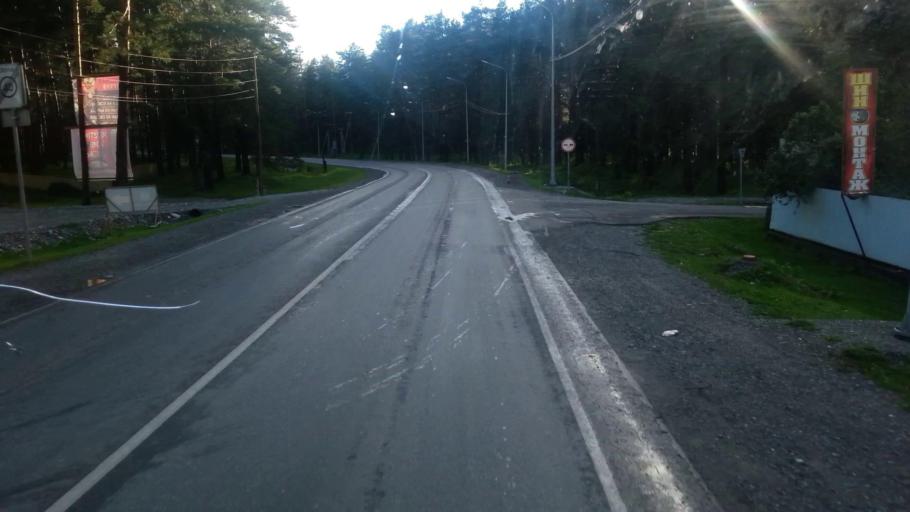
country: RU
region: Altay
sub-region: Mayminskiy Rayon
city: Manzherok
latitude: 51.8334
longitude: 85.7691
